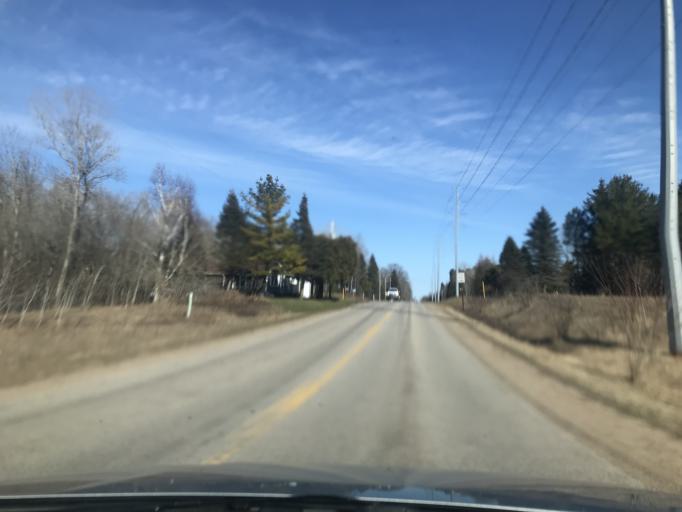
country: US
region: Wisconsin
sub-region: Marinette County
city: Marinette
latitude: 45.1449
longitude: -87.6484
